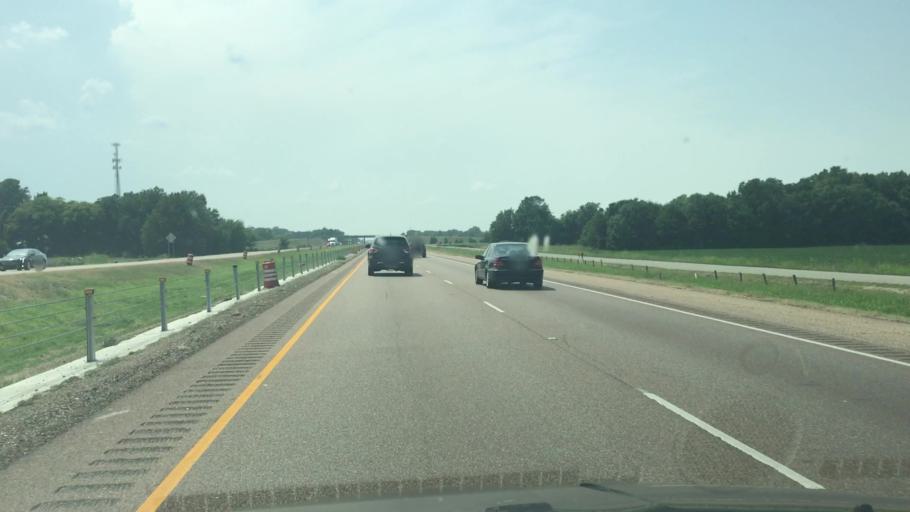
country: US
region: Arkansas
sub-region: Crittenden County
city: Earle
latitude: 35.1496
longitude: -90.3562
